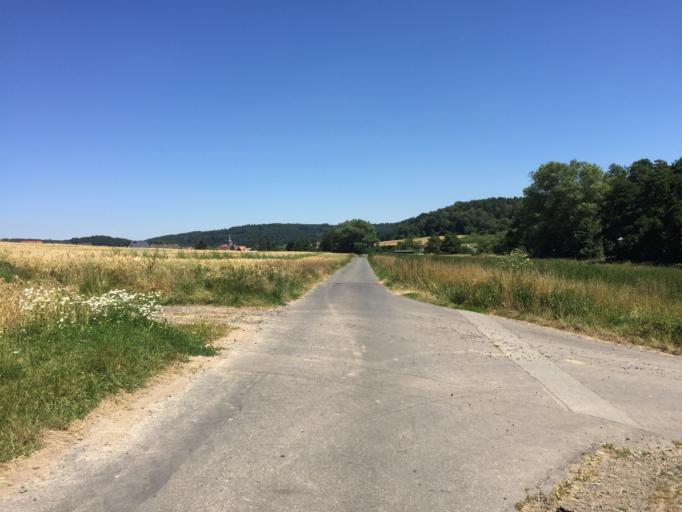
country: DE
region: Hesse
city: Beuern
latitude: 50.6204
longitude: 8.8160
